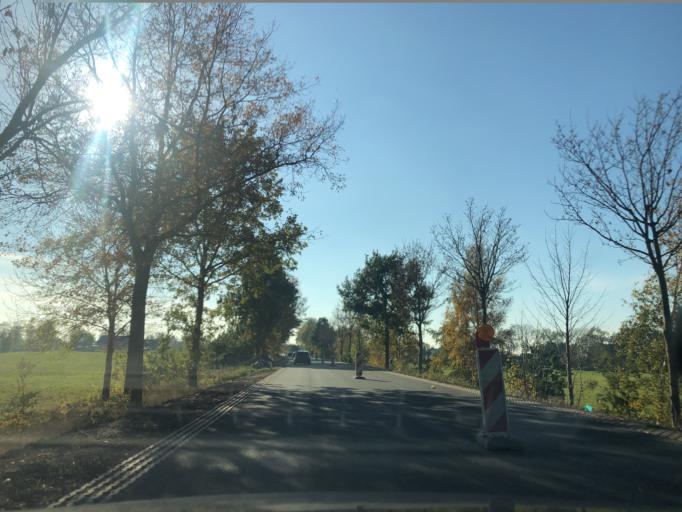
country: DE
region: Lower Saxony
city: Lemwerder
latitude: 53.1520
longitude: 8.5514
